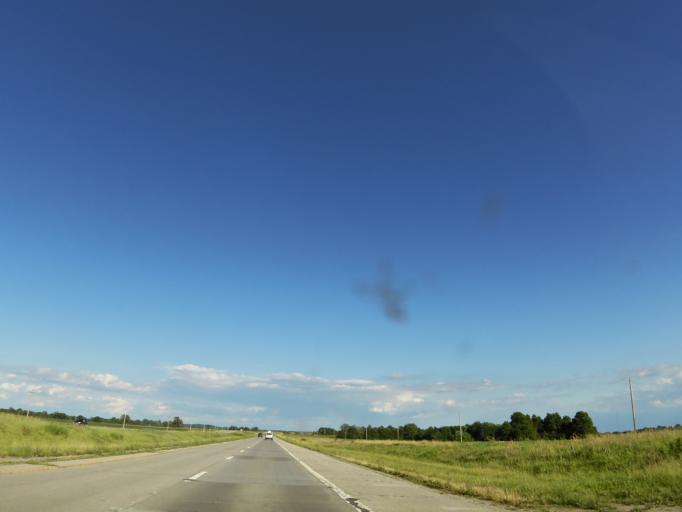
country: US
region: Missouri
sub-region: Pike County
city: Bowling Green
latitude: 39.3116
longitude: -91.1346
